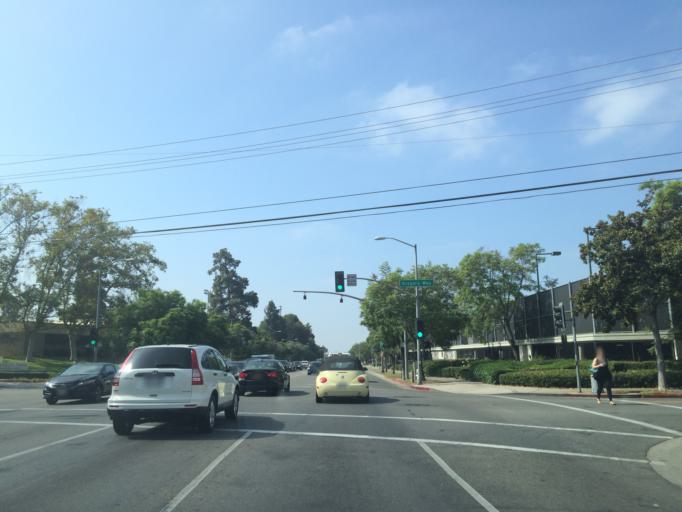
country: US
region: California
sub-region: Los Angeles County
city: Beverly Hills
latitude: 34.0629
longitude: -118.3762
